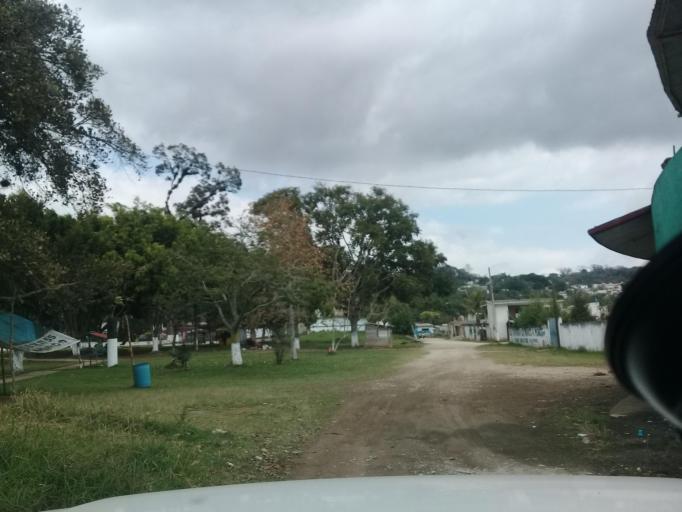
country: MX
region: Veracruz
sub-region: Xalapa
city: Fraccionamiento las Fuentes
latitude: 19.4732
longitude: -96.8804
